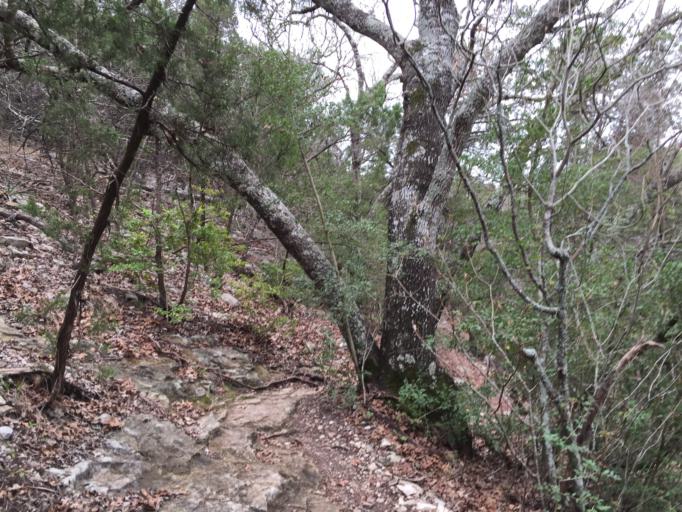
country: US
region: Texas
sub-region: Travis County
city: Rollingwood
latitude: 30.2498
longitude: -97.8203
